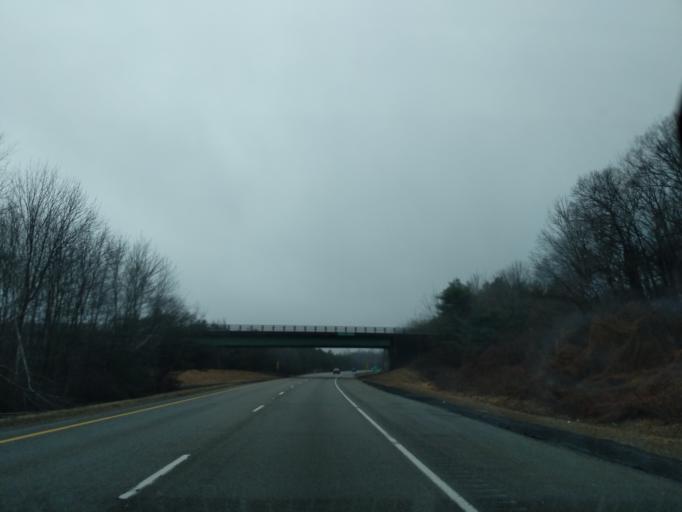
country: US
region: Massachusetts
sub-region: Worcester County
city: Auburn
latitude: 42.1693
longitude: -71.8444
